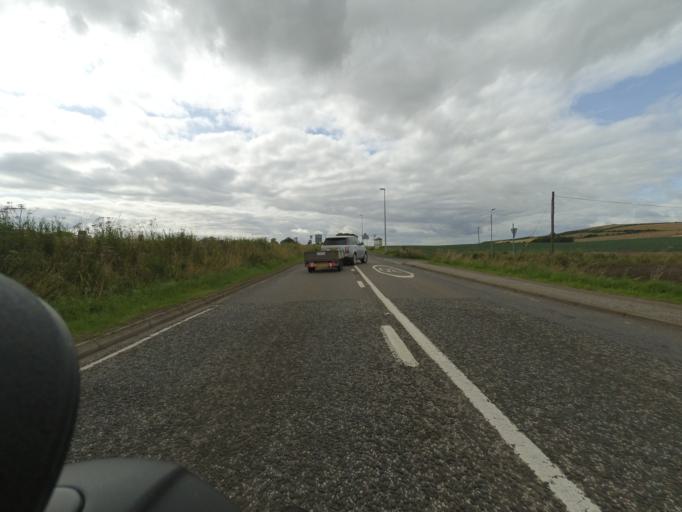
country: GB
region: Scotland
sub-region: Aberdeenshire
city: Laurencekirk
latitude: 56.7709
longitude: -2.4267
